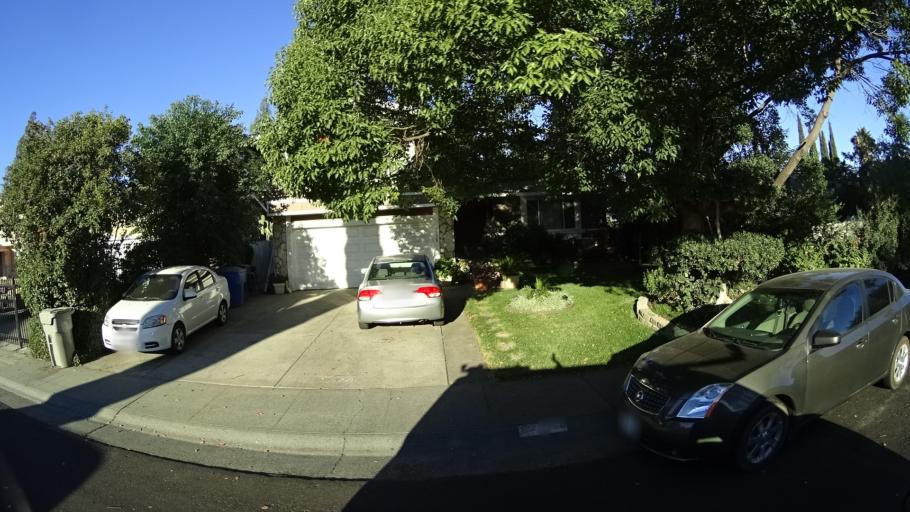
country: US
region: California
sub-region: Sacramento County
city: Parkway
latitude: 38.4904
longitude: -121.4583
